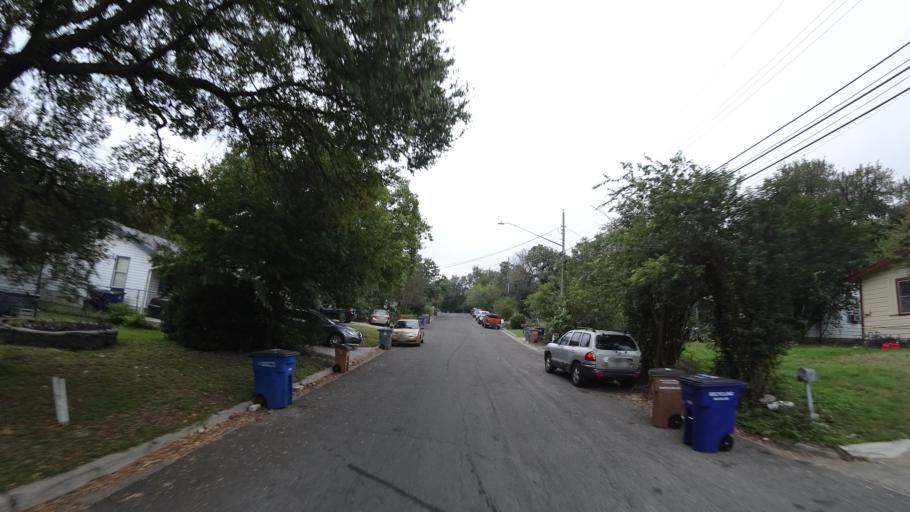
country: US
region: Texas
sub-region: Travis County
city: Austin
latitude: 30.2784
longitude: -97.6963
